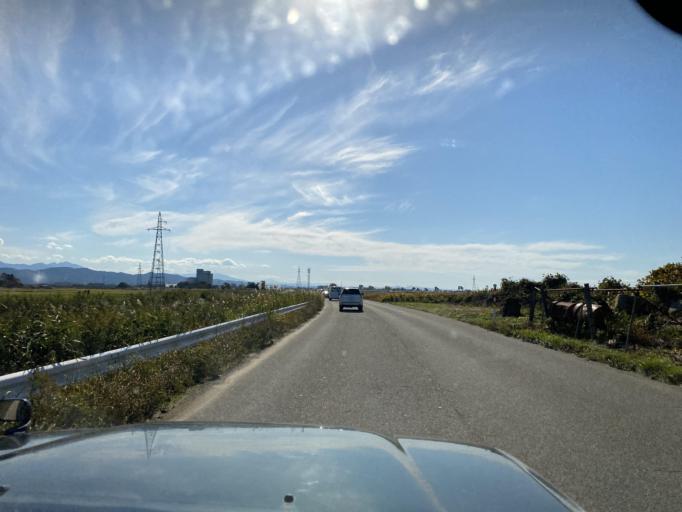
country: JP
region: Niigata
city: Niitsu-honcho
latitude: 37.8016
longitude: 139.0769
